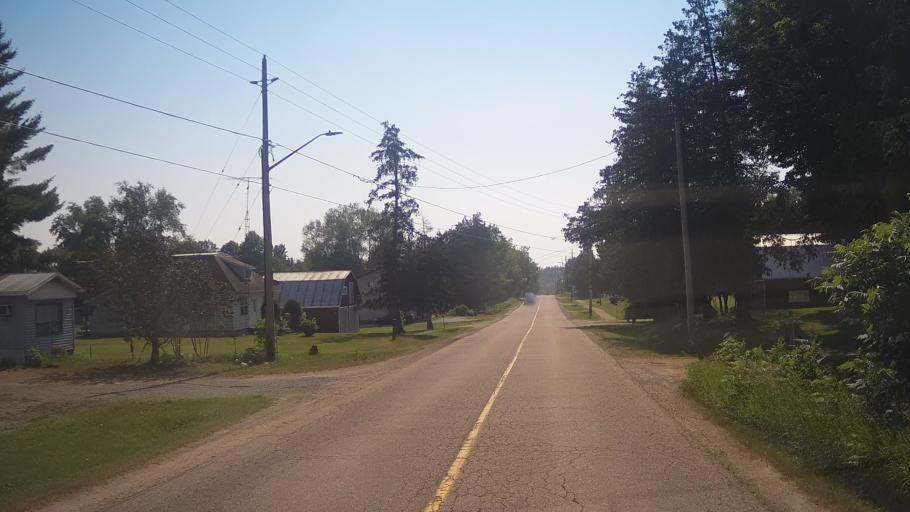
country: CA
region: Ontario
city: Pembroke
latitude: 45.5832
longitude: -77.2360
